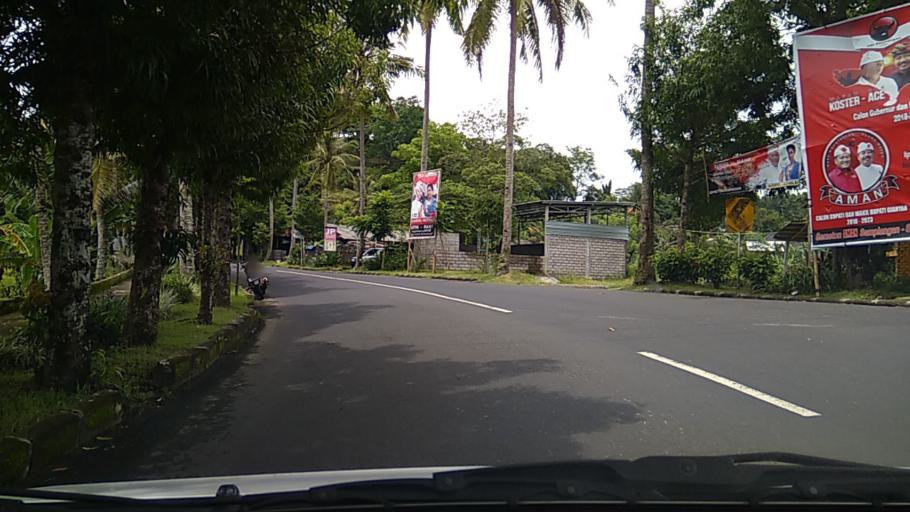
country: ID
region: Bali
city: Banjar Kelodan
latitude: -8.5262
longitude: 115.3476
